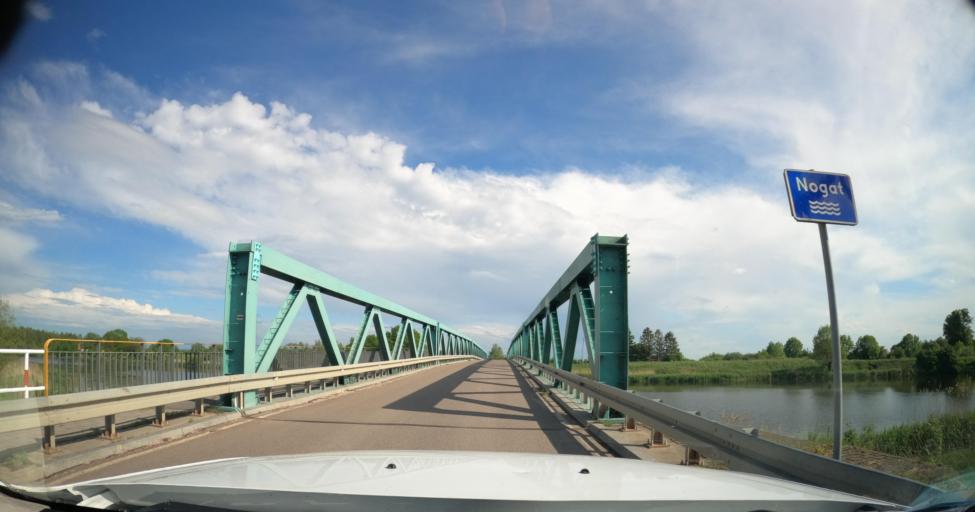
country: PL
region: Warmian-Masurian Voivodeship
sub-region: Powiat elblaski
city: Elblag
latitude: 54.1899
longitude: 19.3140
